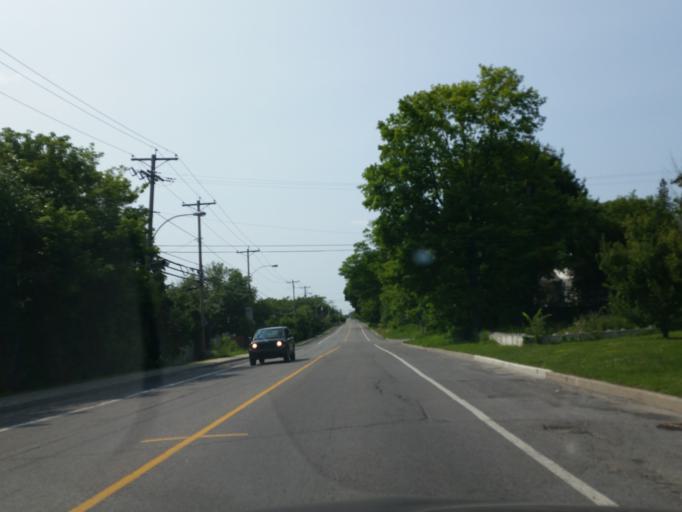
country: CA
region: Ontario
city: Bells Corners
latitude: 45.4026
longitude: -75.8565
